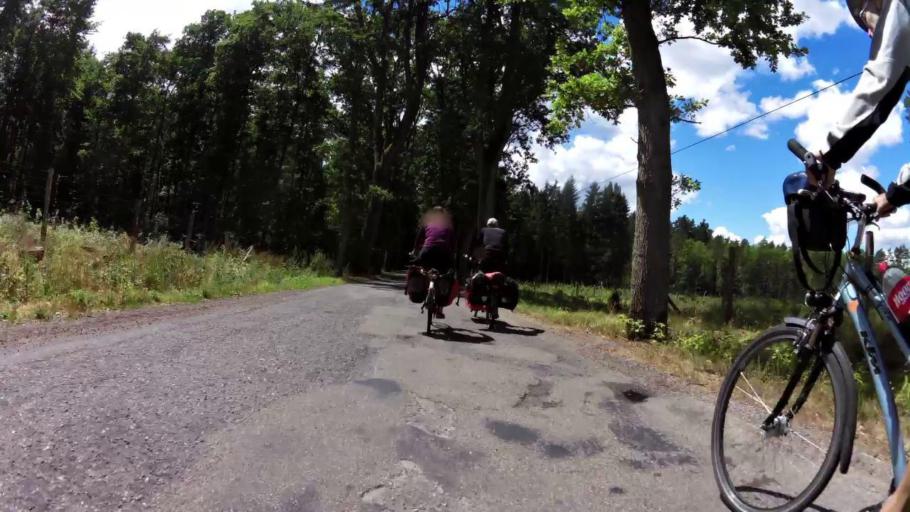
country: PL
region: West Pomeranian Voivodeship
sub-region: Powiat lobeski
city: Resko
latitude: 53.7527
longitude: 15.5058
